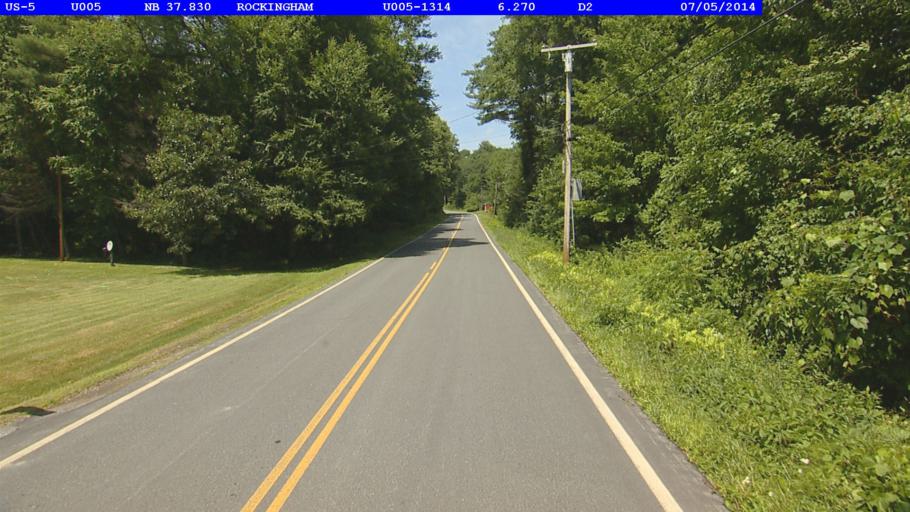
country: US
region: New Hampshire
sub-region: Sullivan County
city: Charlestown
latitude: 43.2052
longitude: -72.4499
